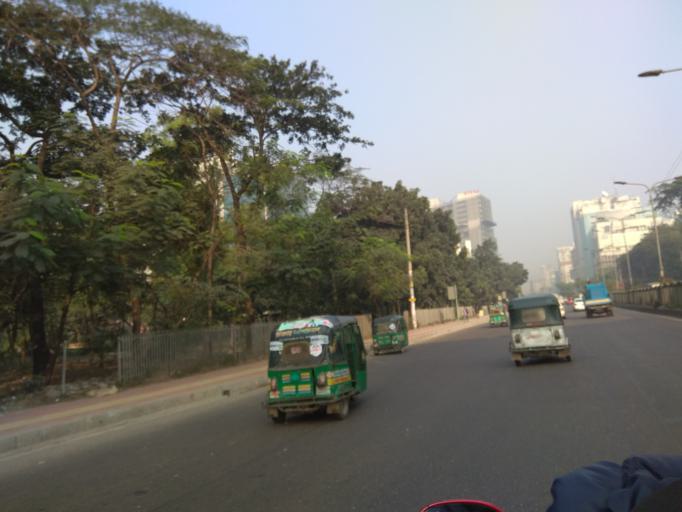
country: BD
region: Dhaka
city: Azimpur
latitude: 23.7474
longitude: 90.3941
